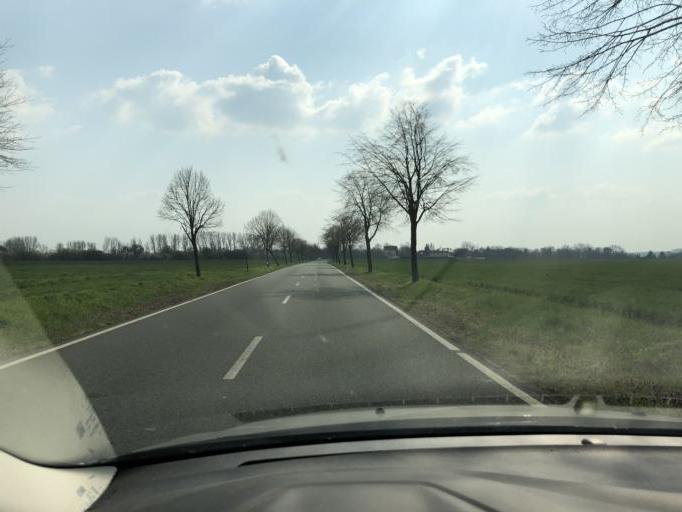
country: DE
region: Saxony-Anhalt
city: Zorbig
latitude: 51.6053
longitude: 12.0674
